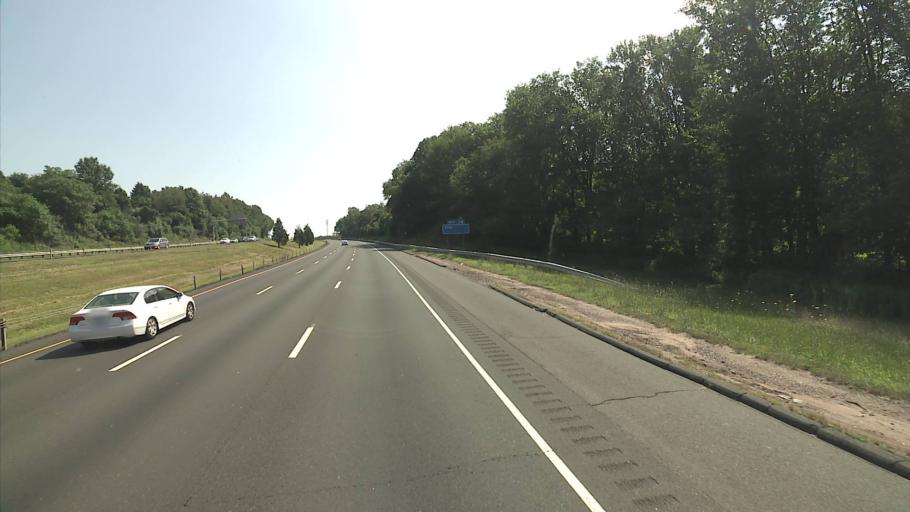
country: US
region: Connecticut
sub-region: New Haven County
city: Wallingford Center
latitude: 41.4301
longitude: -72.8094
